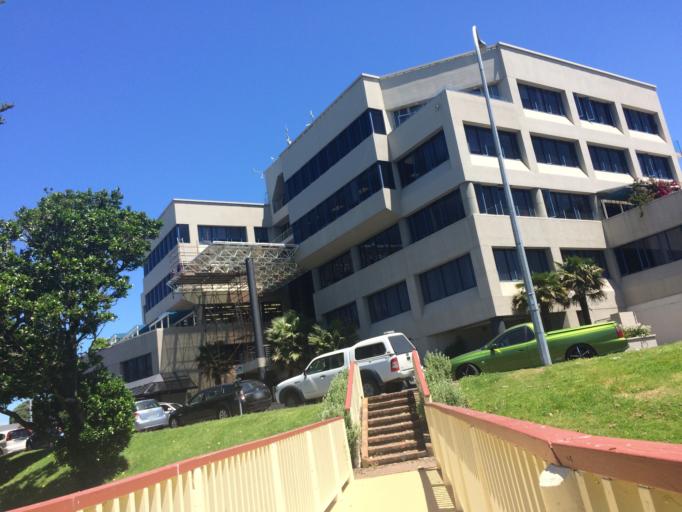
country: NZ
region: Gisborne
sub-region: Gisborne District
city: Gisborne
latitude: -38.6676
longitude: 178.0290
